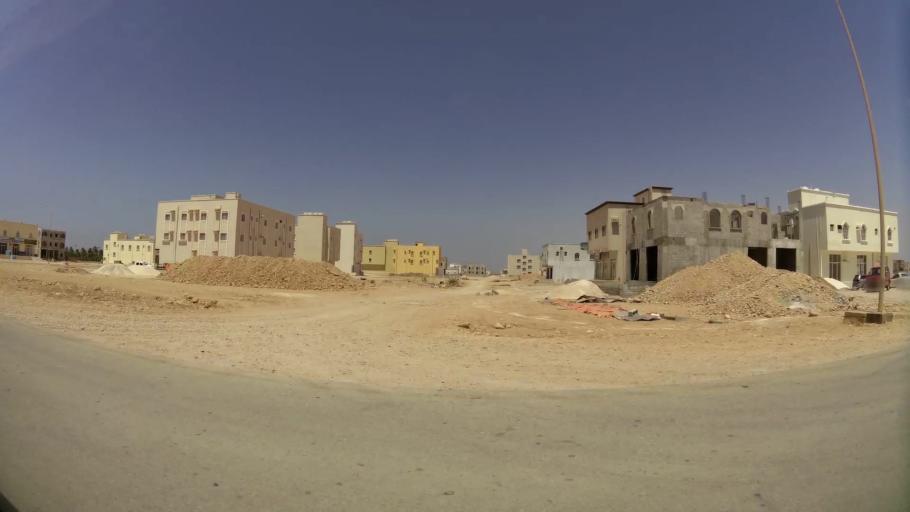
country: OM
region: Zufar
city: Salalah
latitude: 17.0511
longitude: 54.2123
